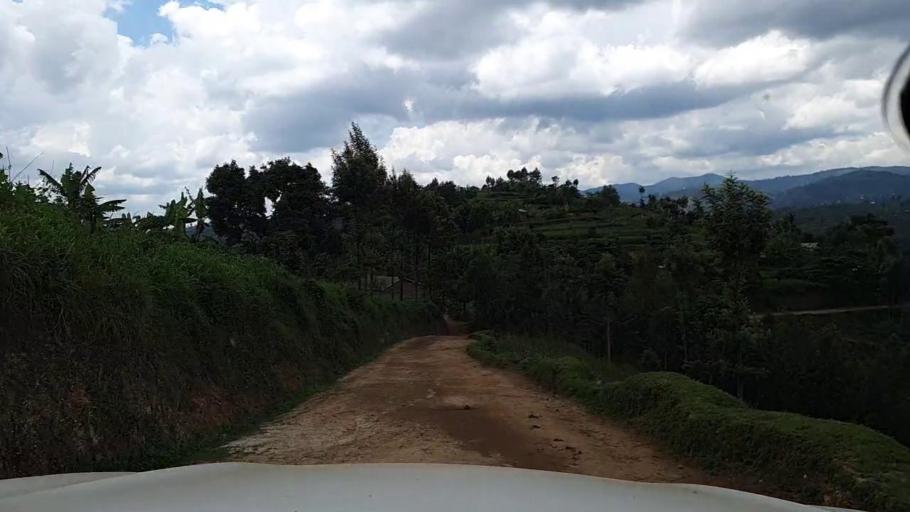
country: RW
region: Southern Province
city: Nzega
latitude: -2.6376
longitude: 29.4842
